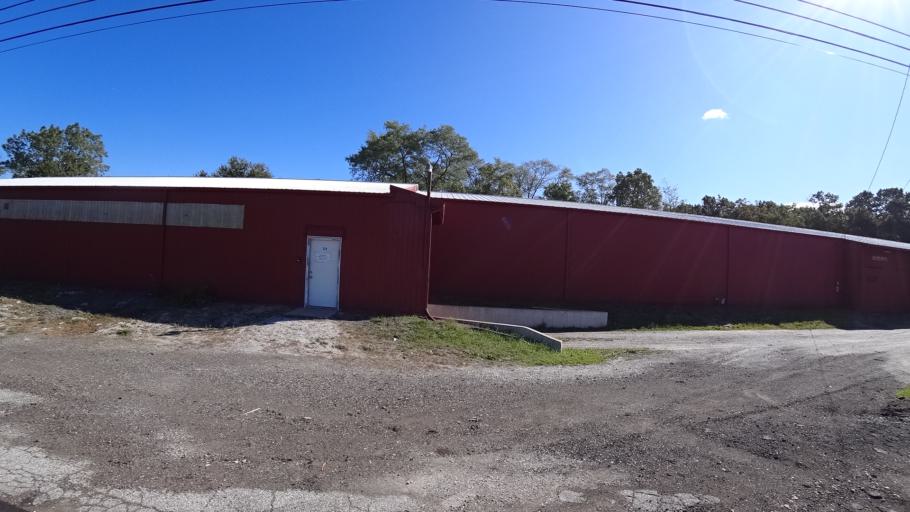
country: US
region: Indiana
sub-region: LaPorte County
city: Michigan City
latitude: 41.7016
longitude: -86.9141
